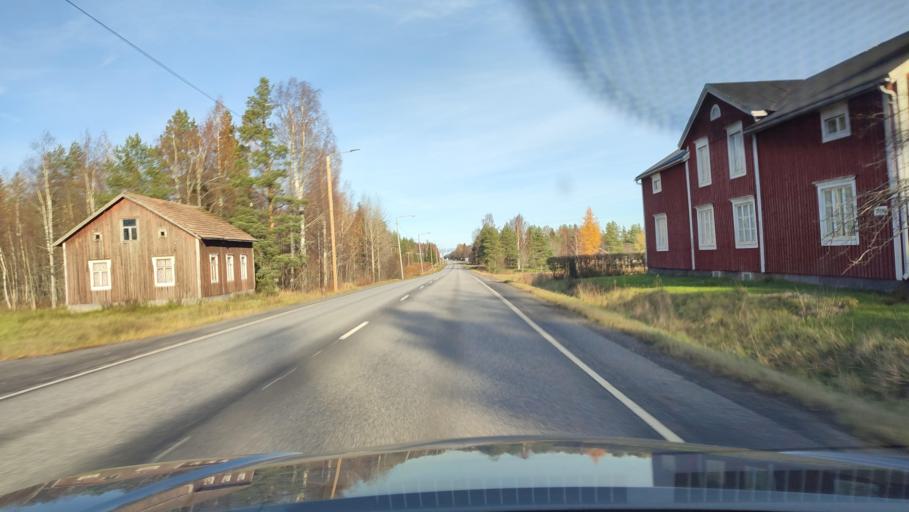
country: FI
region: Ostrobothnia
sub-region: Vaasa
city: Malax
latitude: 62.7723
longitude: 21.6587
